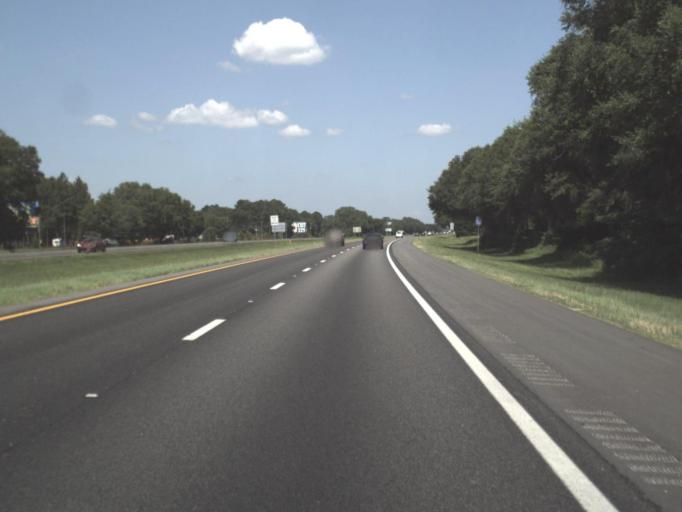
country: US
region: Florida
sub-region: Madison County
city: Madison
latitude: 30.3969
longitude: -83.3638
